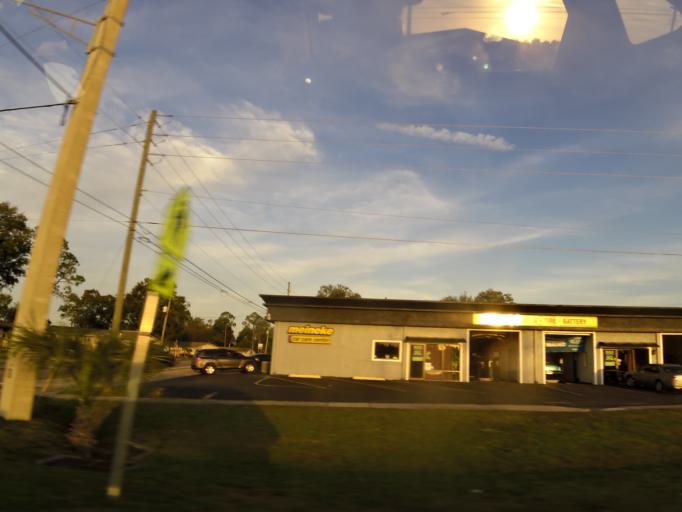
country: US
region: Florida
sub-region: Volusia County
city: De Land Southwest
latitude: 29.0061
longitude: -81.3026
